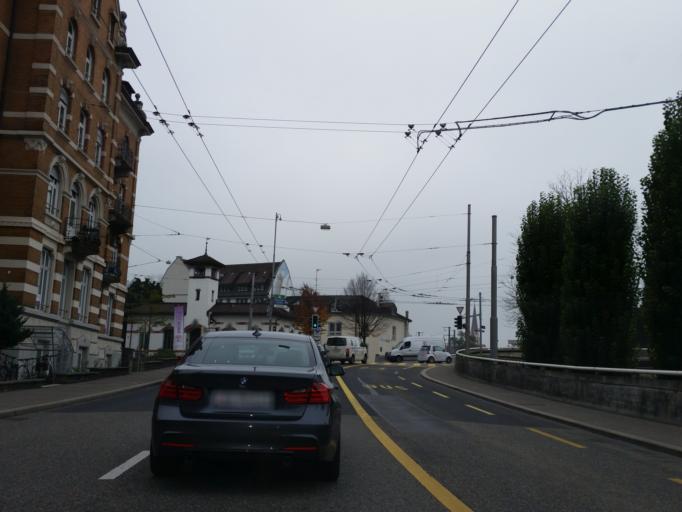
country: CH
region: Saint Gallen
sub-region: Wahlkreis St. Gallen
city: Sankt Gallen
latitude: 47.4207
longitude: 9.3669
